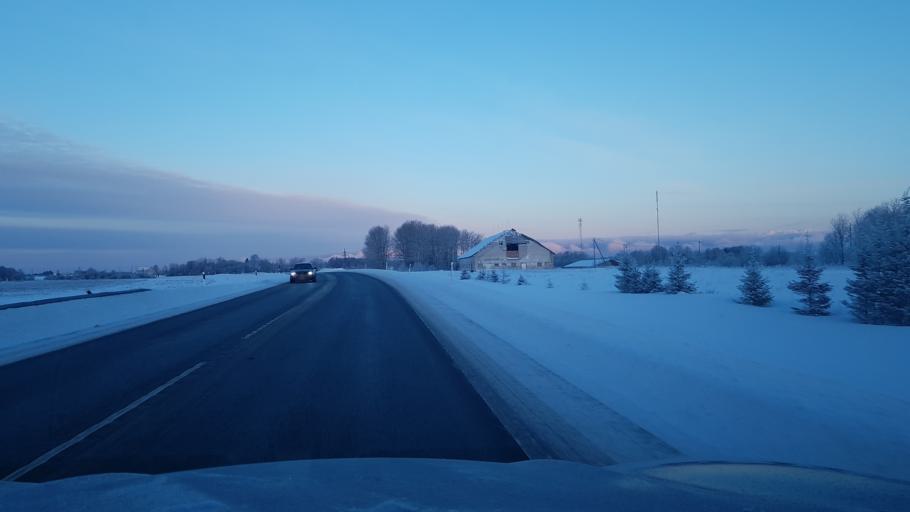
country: EE
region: Ida-Virumaa
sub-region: Narva-Joesuu linn
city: Narva-Joesuu
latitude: 59.3982
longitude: 28.0752
